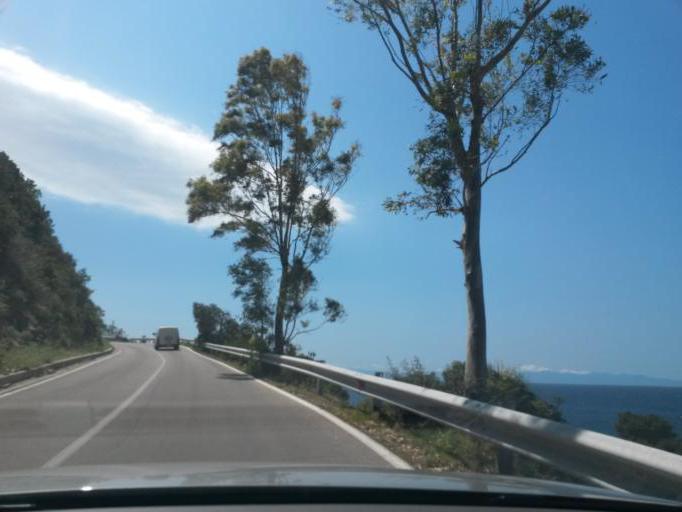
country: IT
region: Tuscany
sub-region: Provincia di Livorno
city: Marciana
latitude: 42.7466
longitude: 10.1214
